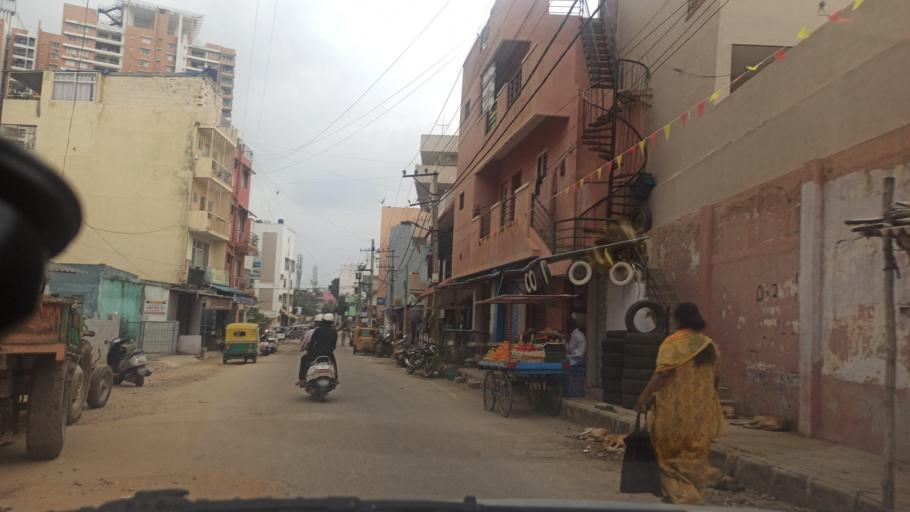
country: IN
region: Karnataka
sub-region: Bangalore Urban
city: Yelahanka
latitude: 13.0481
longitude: 77.6010
